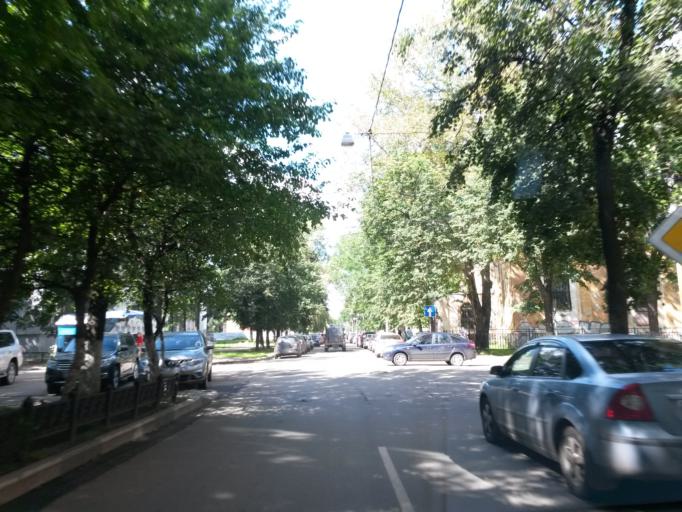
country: RU
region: Jaroslavl
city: Yaroslavl
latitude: 57.6301
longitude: 39.8750
